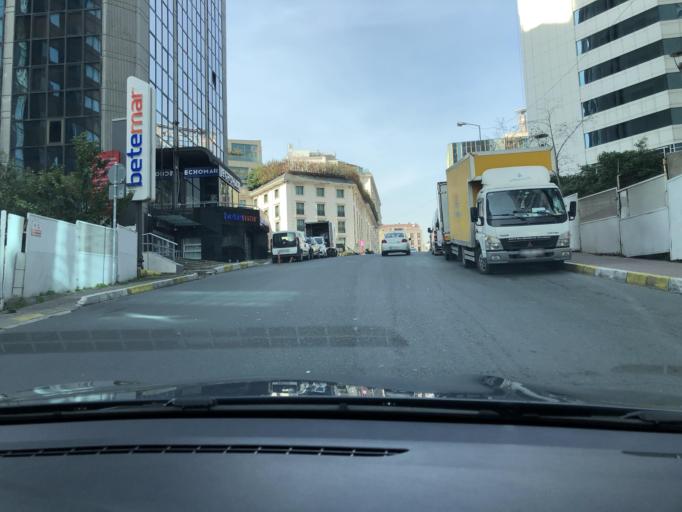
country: TR
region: Istanbul
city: Sisli
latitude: 41.0603
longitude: 28.9904
